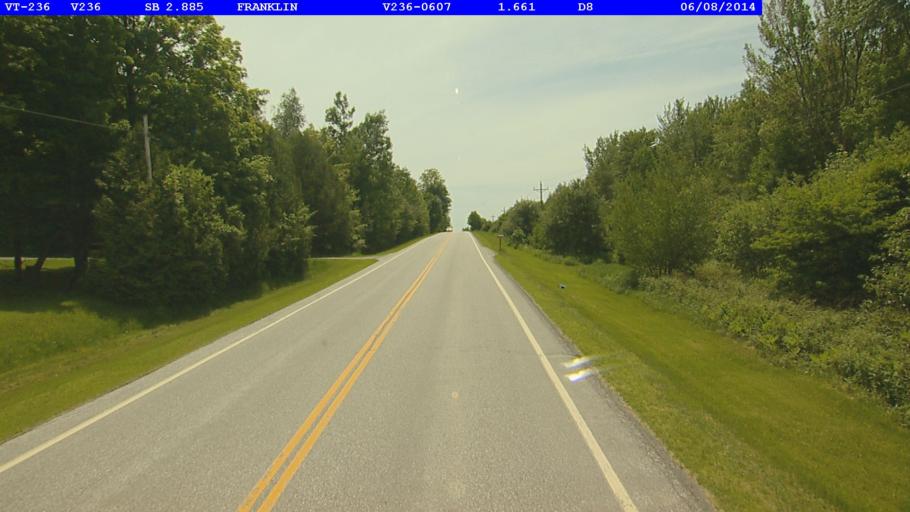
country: US
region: Vermont
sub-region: Franklin County
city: Enosburg Falls
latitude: 44.9518
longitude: -72.8629
